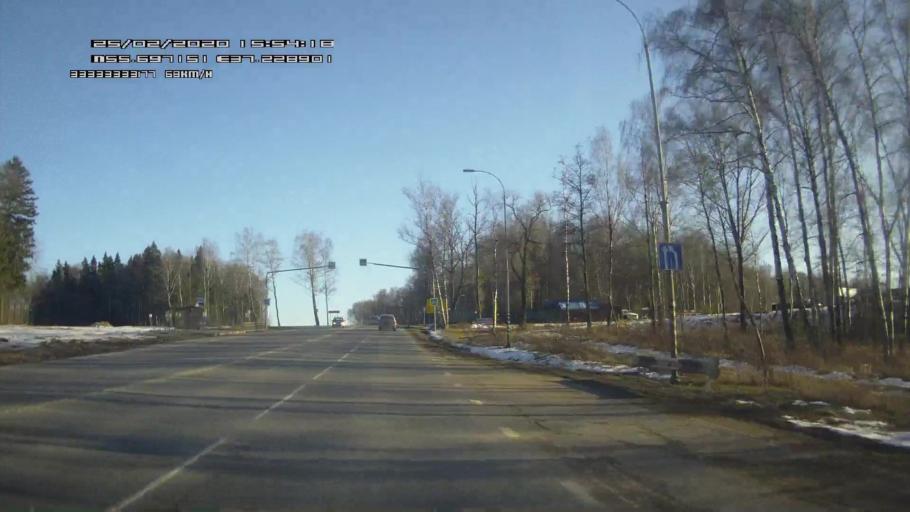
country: RU
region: Moskovskaya
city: Odintsovo
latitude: 55.6974
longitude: 37.2288
